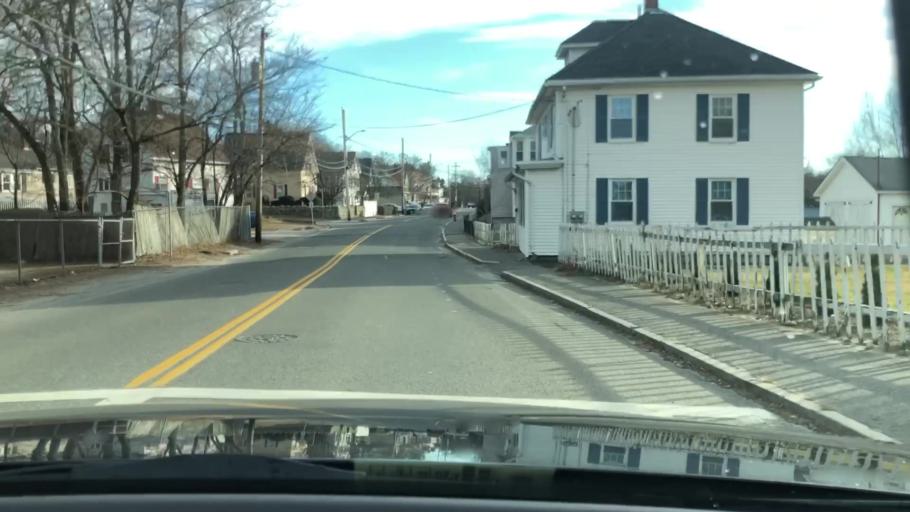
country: US
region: Massachusetts
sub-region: Worcester County
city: Milford
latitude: 42.1409
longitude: -71.5120
